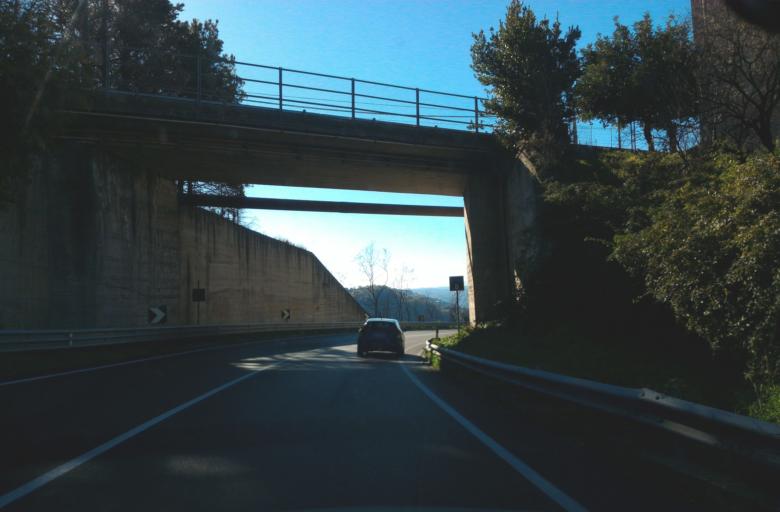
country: IT
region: Calabria
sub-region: Provincia di Cosenza
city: Rovito
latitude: 39.3013
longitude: 16.3138
